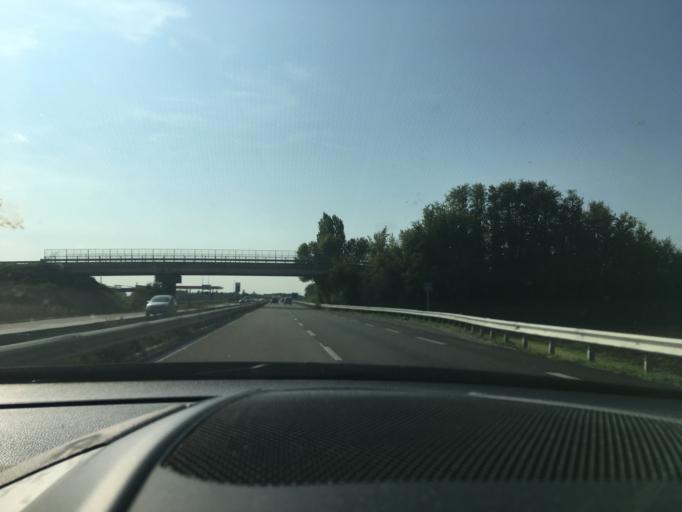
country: IT
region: Emilia-Romagna
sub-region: Provincia di Rimini
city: Bellaria-Igea Marina
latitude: 44.1202
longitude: 12.4732
